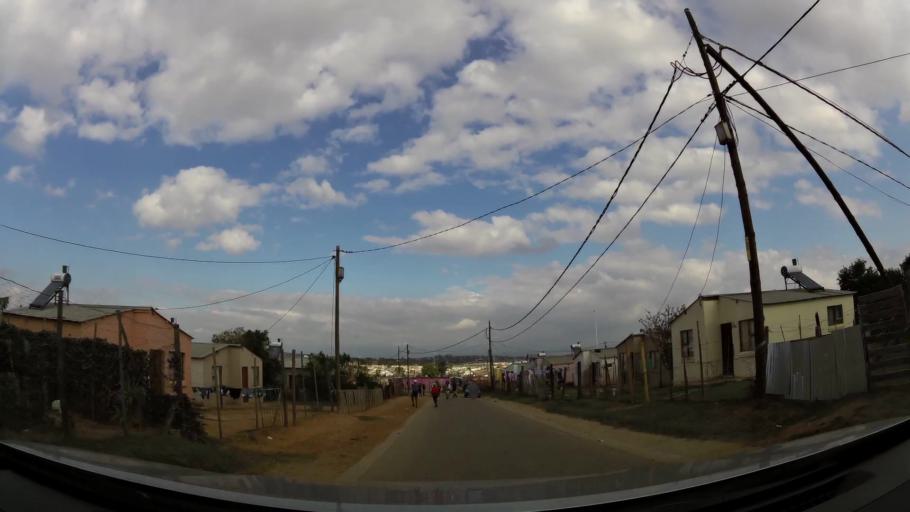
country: ZA
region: Eastern Cape
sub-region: Nelson Mandela Bay Metropolitan Municipality
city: Uitenhage
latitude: -33.7312
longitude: 25.3938
